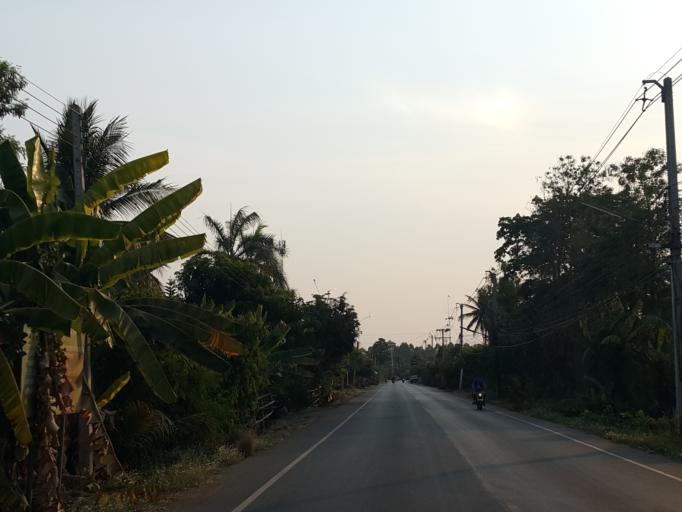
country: TH
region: Sukhothai
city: Si Samrong
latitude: 17.2115
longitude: 99.8705
